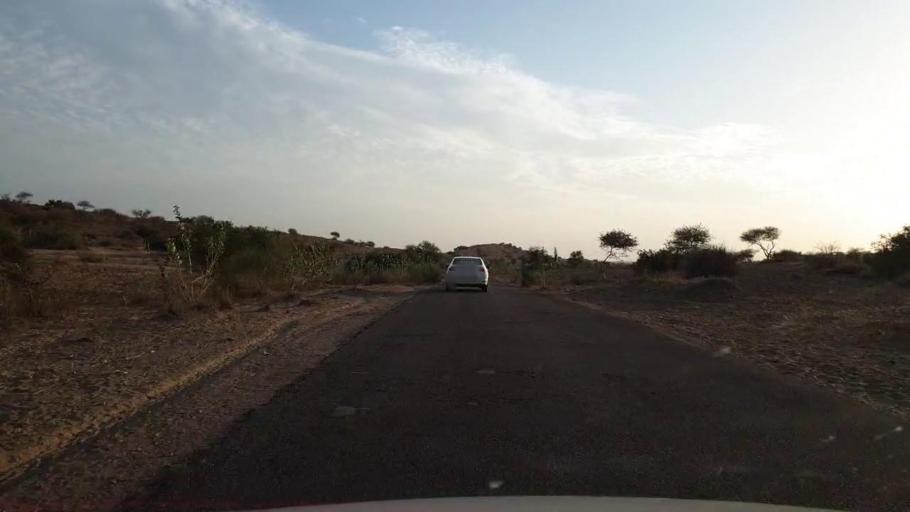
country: PK
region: Sindh
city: Nabisar
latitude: 25.0219
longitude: 69.9422
